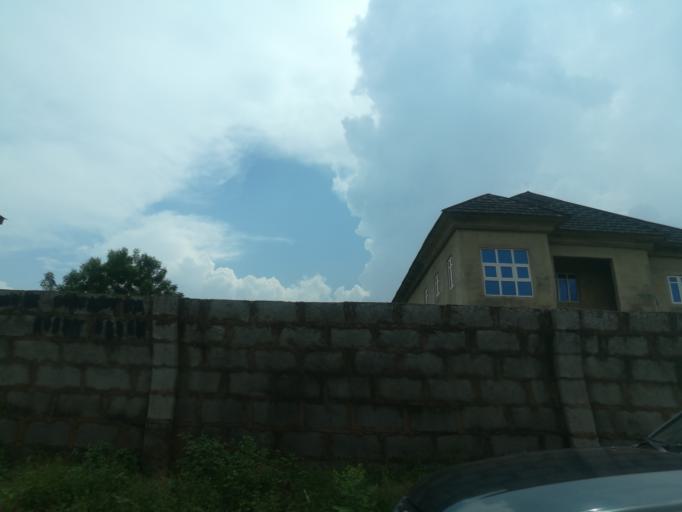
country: NG
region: Oyo
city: Ibadan
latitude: 7.4270
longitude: 3.9140
